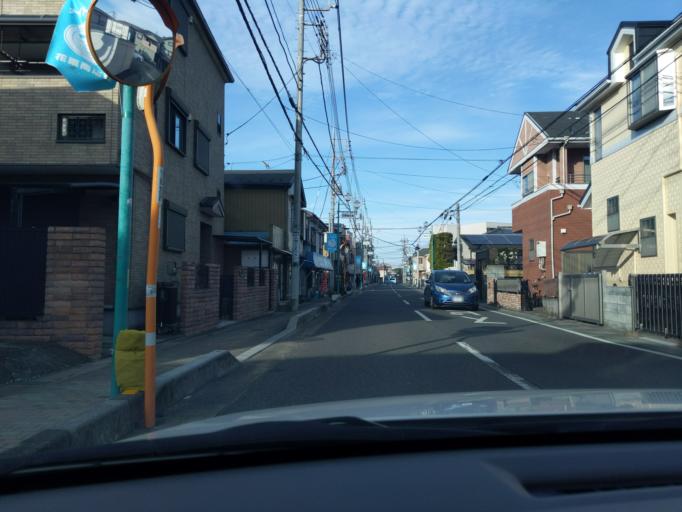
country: JP
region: Saitama
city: Soka
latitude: 35.8368
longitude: 139.7915
